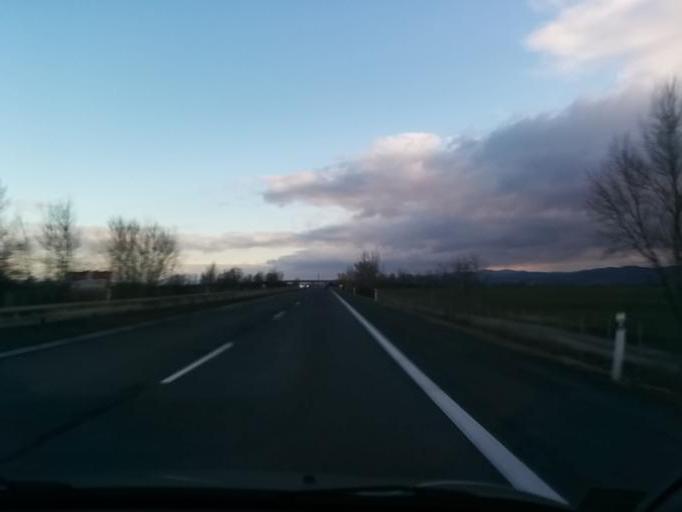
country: SK
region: Trnavsky
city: Leopoldov
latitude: 48.5148
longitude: 17.7738
